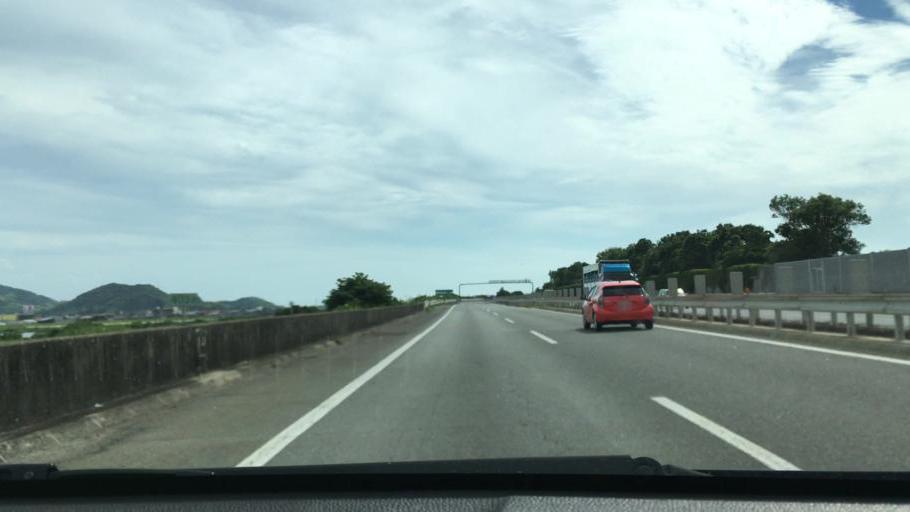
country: JP
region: Yamaguchi
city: Hofu
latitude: 34.0606
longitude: 131.5445
